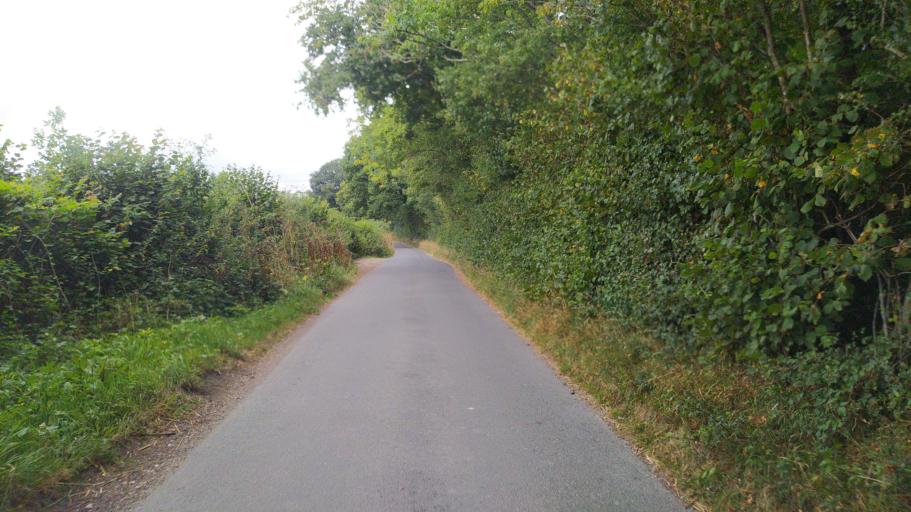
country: GB
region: England
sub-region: Hampshire
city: Petersfield
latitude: 50.9882
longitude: -0.9732
